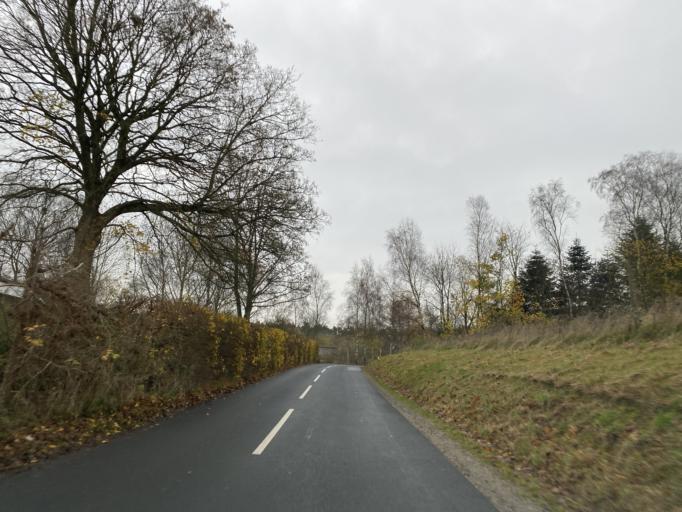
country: DK
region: Central Jutland
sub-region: Silkeborg Kommune
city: Svejbaek
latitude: 56.1572
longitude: 9.6844
